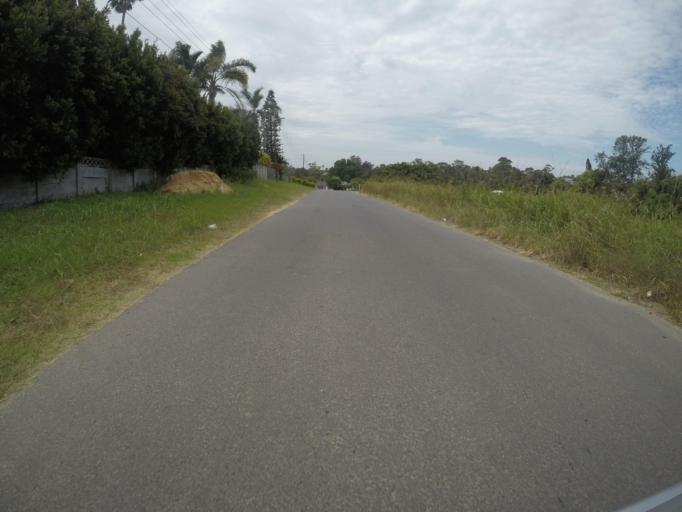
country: ZA
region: Eastern Cape
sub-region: Buffalo City Metropolitan Municipality
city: East London
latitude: -32.9932
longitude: 27.8721
